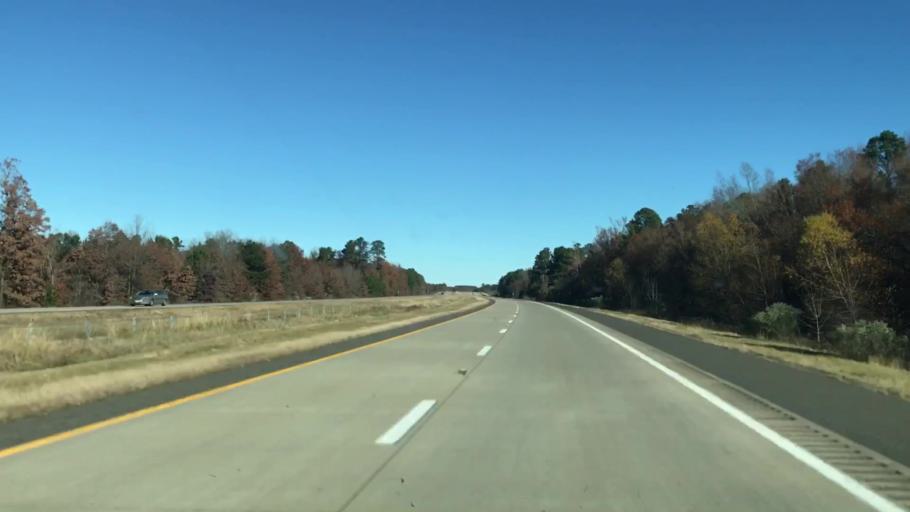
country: US
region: Texas
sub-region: Bowie County
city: Texarkana
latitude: 33.2139
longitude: -93.8736
